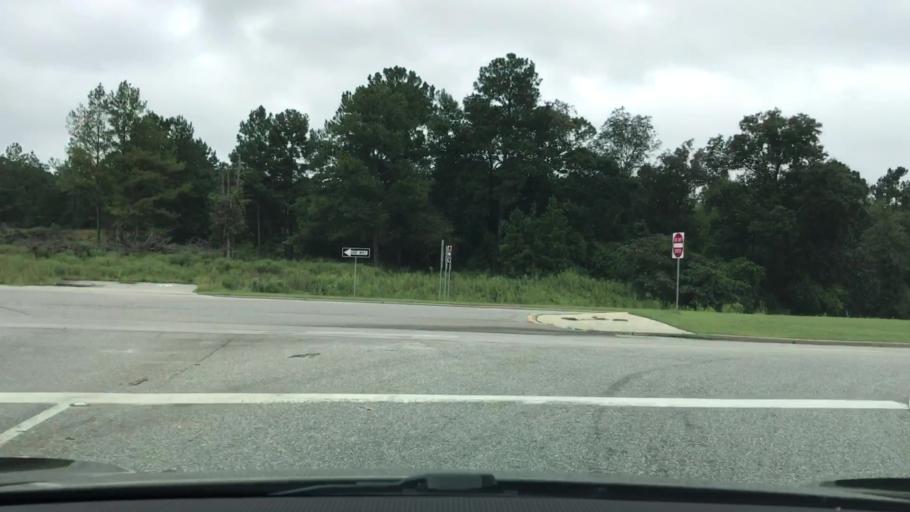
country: US
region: Alabama
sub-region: Coffee County
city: Elba
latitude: 31.4181
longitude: -86.0873
